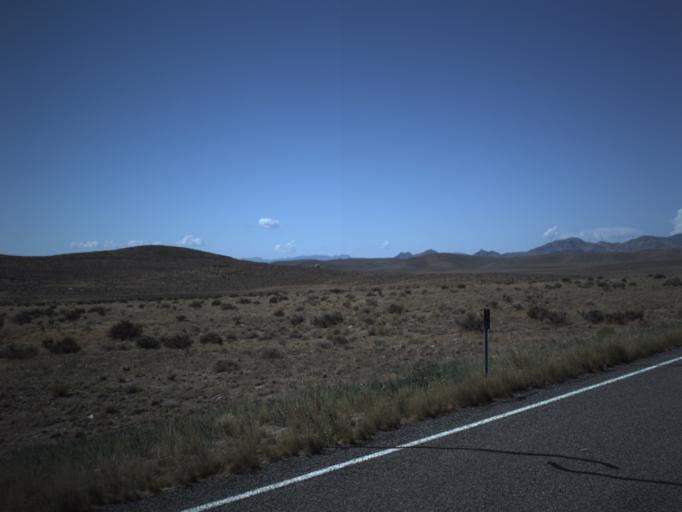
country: US
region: Utah
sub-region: Beaver County
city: Milford
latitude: 39.0464
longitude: -113.2839
